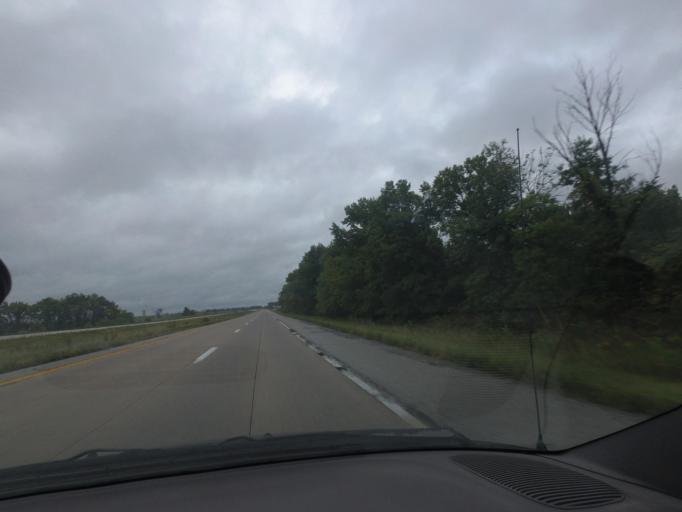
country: US
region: Missouri
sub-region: Marion County
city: Monroe City
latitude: 39.6714
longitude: -91.8568
